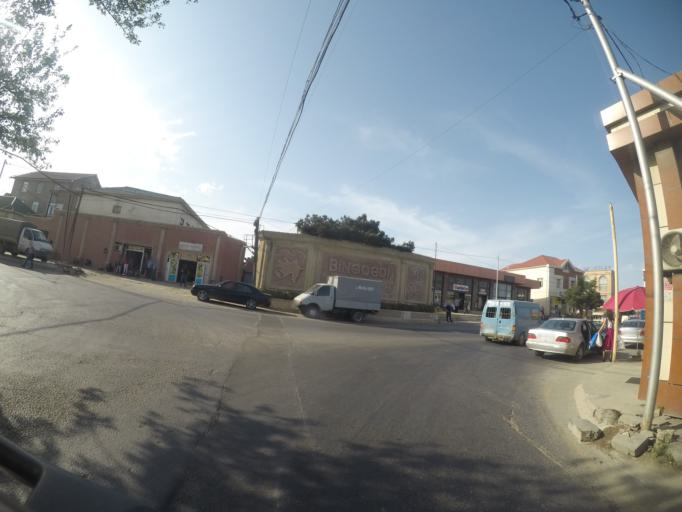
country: AZ
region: Baki
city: Binagadi
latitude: 40.4671
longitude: 49.8416
